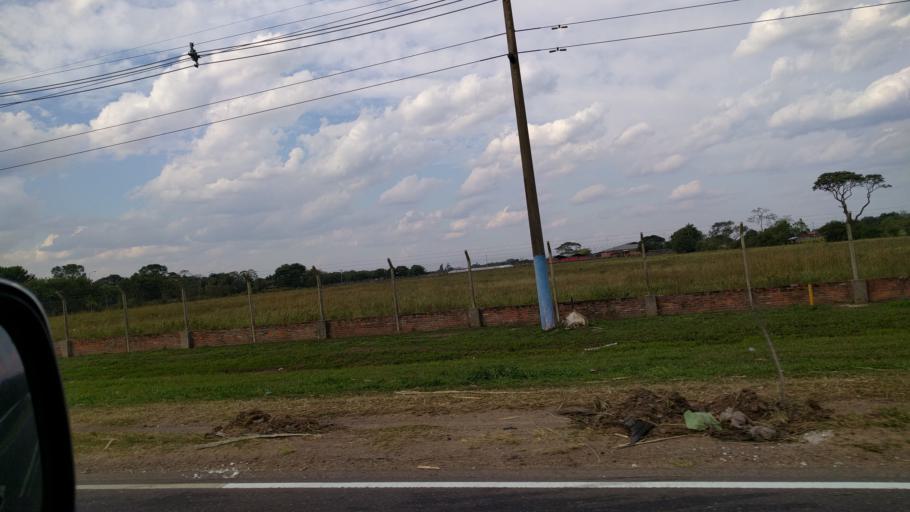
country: BO
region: Santa Cruz
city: Warnes
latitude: -17.5534
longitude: -63.1598
